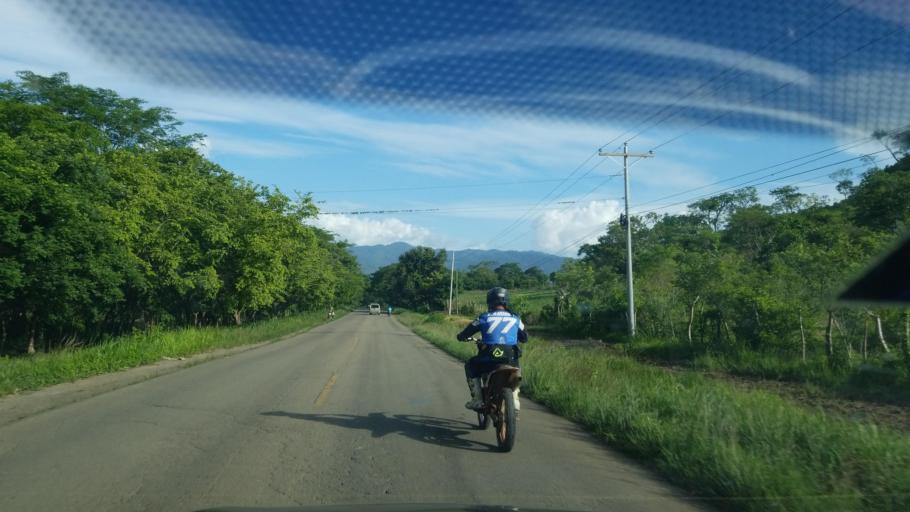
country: HN
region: El Paraiso
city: Cuyali
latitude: 13.9144
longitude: -86.5571
